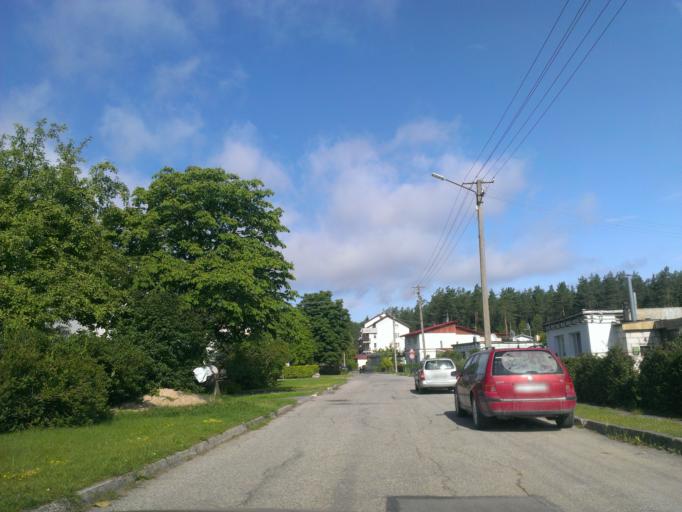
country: LV
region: Incukalns
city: Vangazi
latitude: 57.0955
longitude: 24.5483
